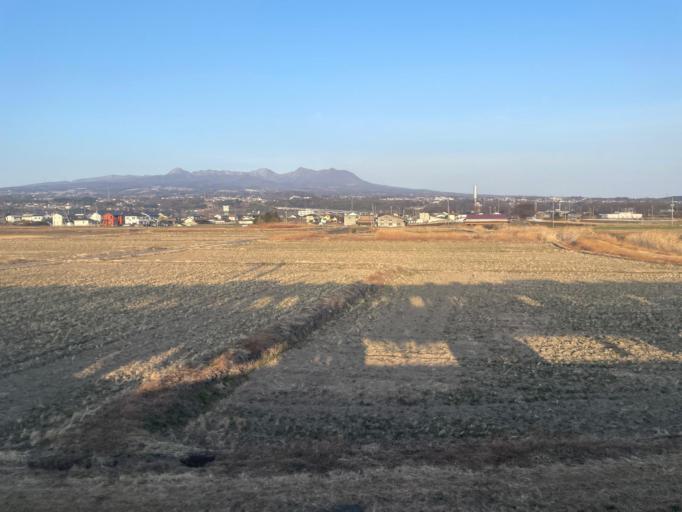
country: JP
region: Gunma
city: Shibukawa
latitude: 36.4782
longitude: 139.0075
